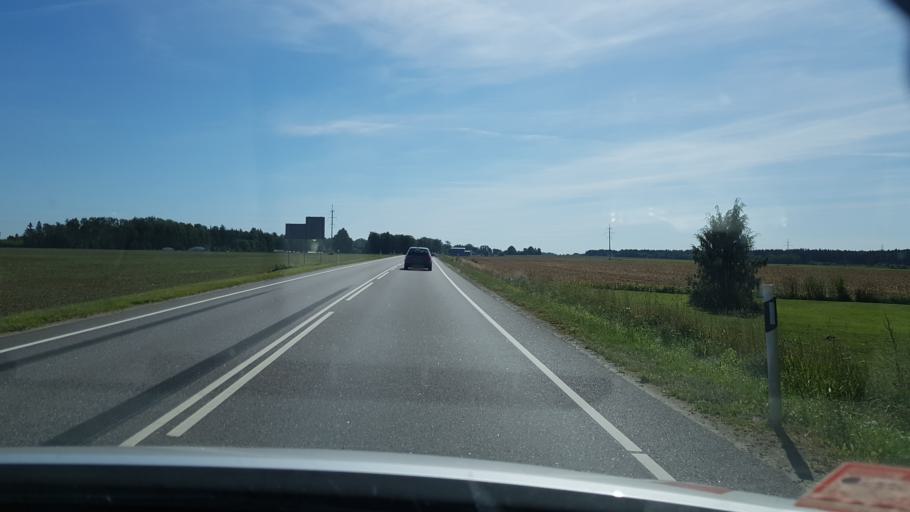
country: EE
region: Tartu
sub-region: Tartu linn
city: Tartu
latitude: 58.4182
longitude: 26.8752
